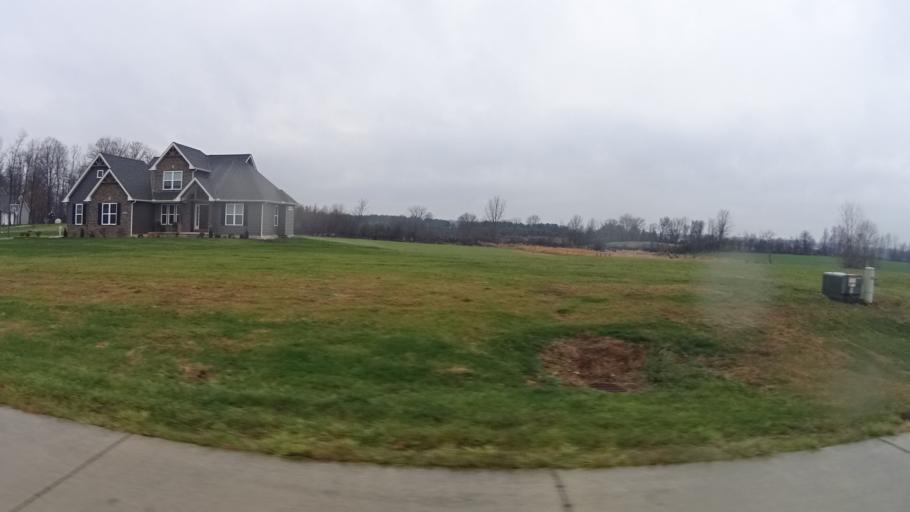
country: US
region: Ohio
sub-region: Lorain County
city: Lagrange
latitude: 41.2313
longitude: -82.1464
